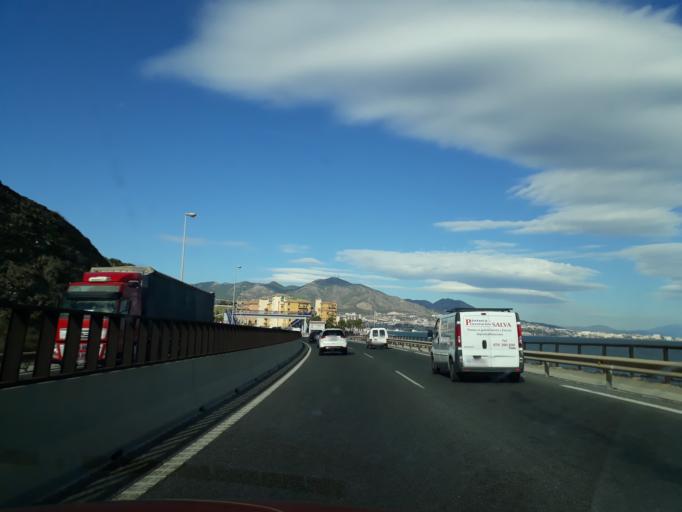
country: ES
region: Andalusia
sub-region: Provincia de Malaga
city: Fuengirola
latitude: 36.5181
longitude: -4.6305
